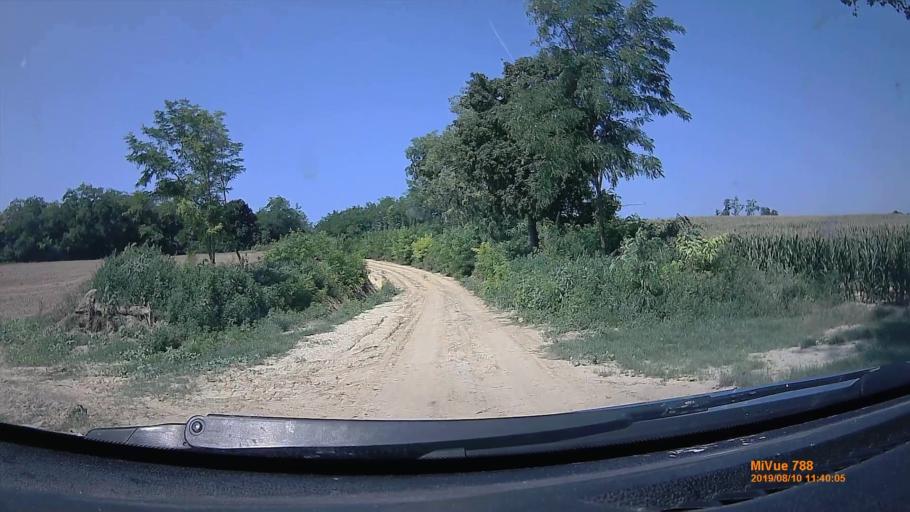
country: HU
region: Somogy
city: Somogyvar
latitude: 46.5156
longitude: 17.7707
